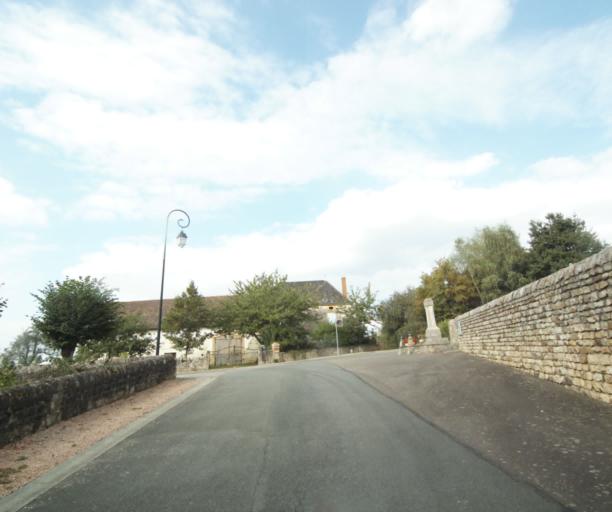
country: FR
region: Bourgogne
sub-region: Departement de Saone-et-Loire
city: Palinges
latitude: 46.5101
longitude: 4.2649
